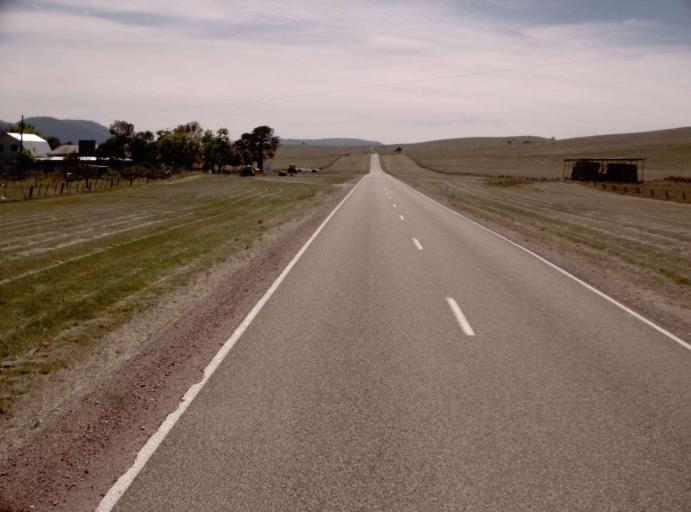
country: AU
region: Victoria
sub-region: Alpine
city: Mount Beauty
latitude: -36.9961
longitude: 147.6809
